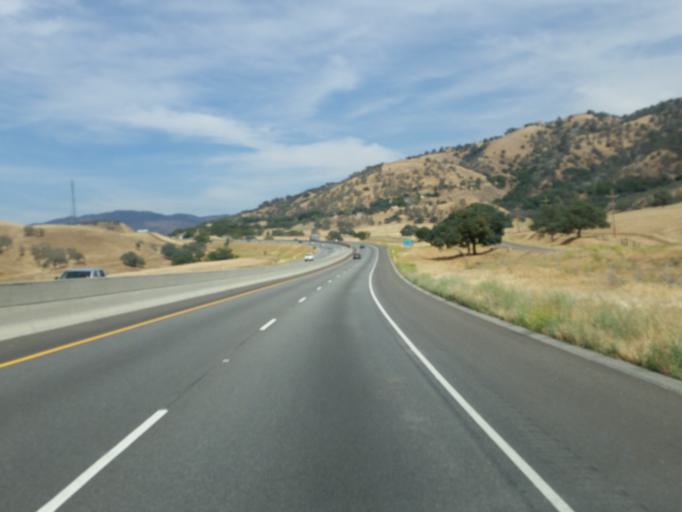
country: US
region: California
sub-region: Kern County
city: Bear Valley Springs
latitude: 35.2638
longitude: -118.6460
